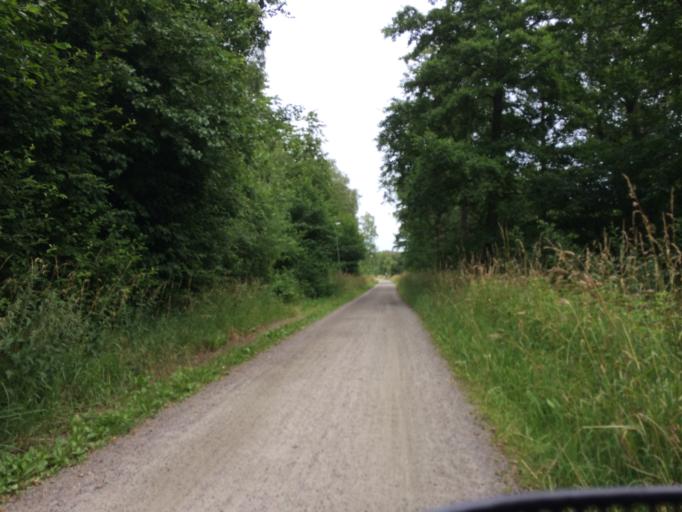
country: SE
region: Skane
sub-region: Vellinge Kommun
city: Ljunghusen
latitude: 55.4064
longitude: 12.9026
